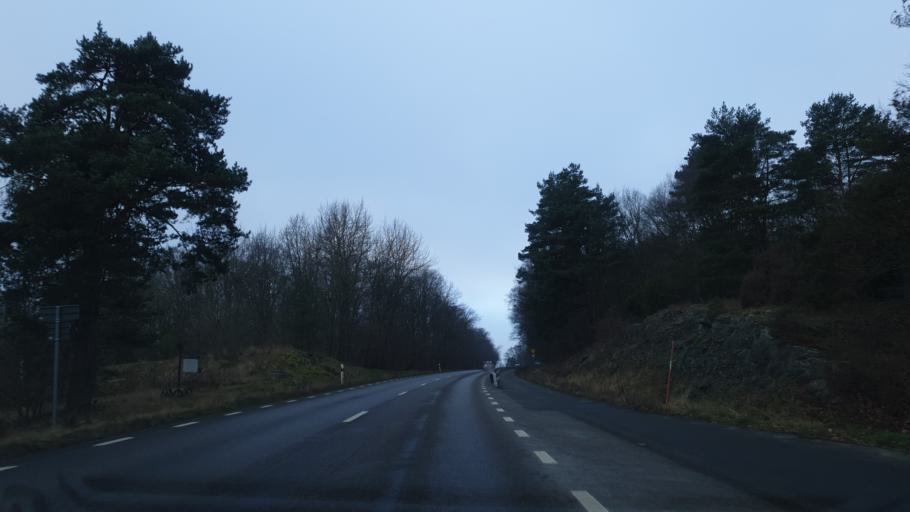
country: SE
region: Blekinge
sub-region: Solvesborgs Kommun
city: Soelvesborg
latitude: 56.0945
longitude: 14.6575
